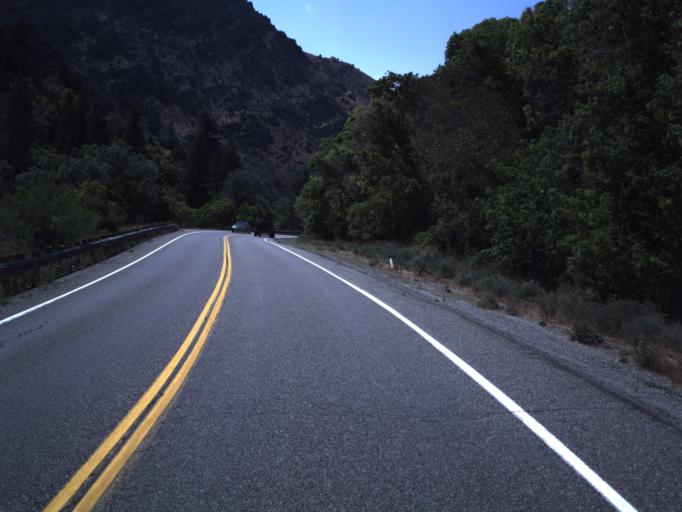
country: US
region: Utah
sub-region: Cache County
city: North Logan
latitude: 41.7430
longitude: -111.7648
